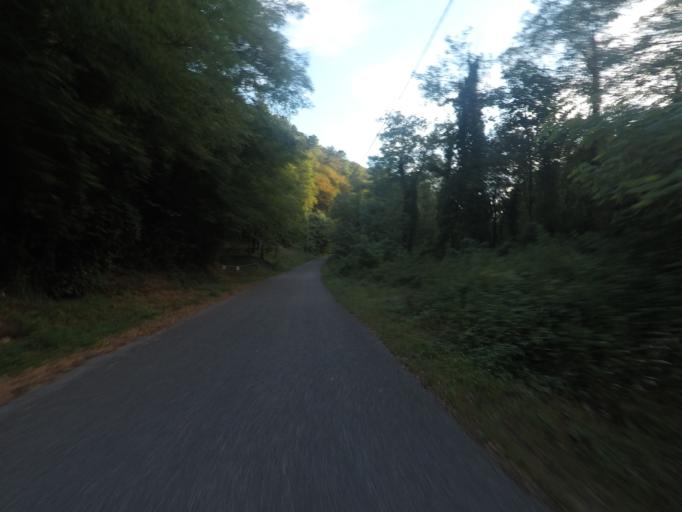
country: IT
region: Tuscany
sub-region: Provincia di Lucca
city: Pescaglia
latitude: 43.9454
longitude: 10.4060
